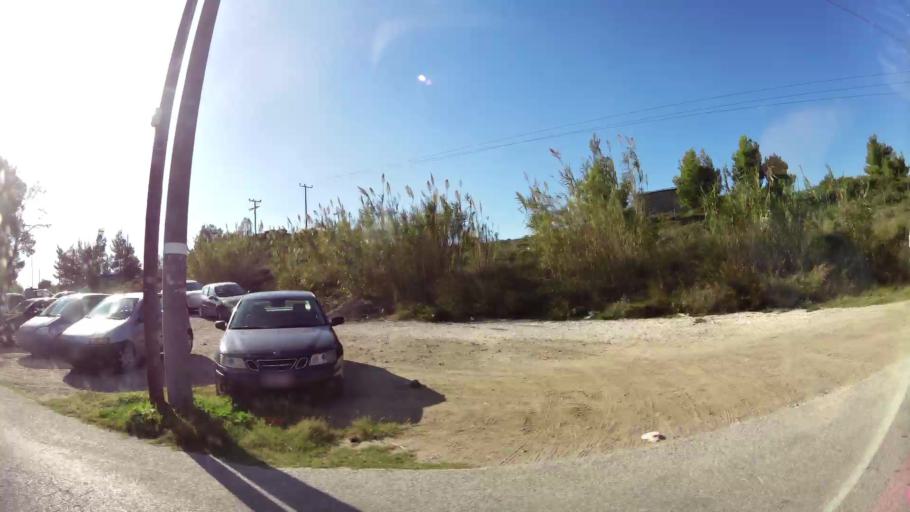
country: GR
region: Attica
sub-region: Nomarchia Anatolikis Attikis
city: Anthousa
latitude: 38.0370
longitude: 23.8820
